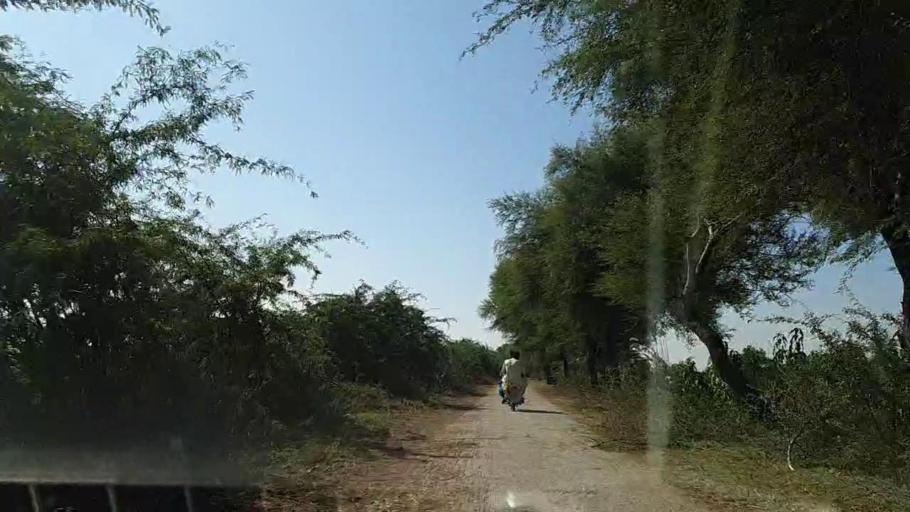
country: PK
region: Sindh
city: Chuhar Jamali
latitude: 24.5783
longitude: 68.0463
